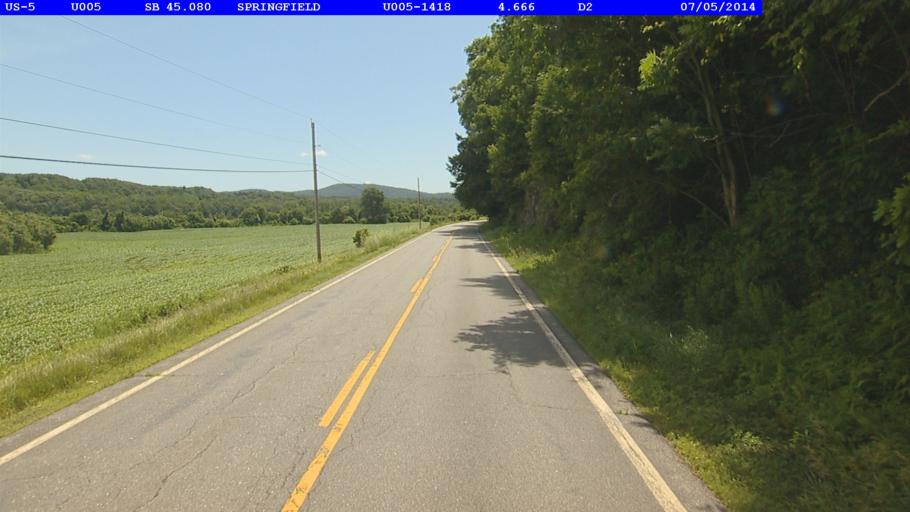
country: US
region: New Hampshire
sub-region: Sullivan County
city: Charlestown
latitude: 43.2809
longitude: -72.4136
